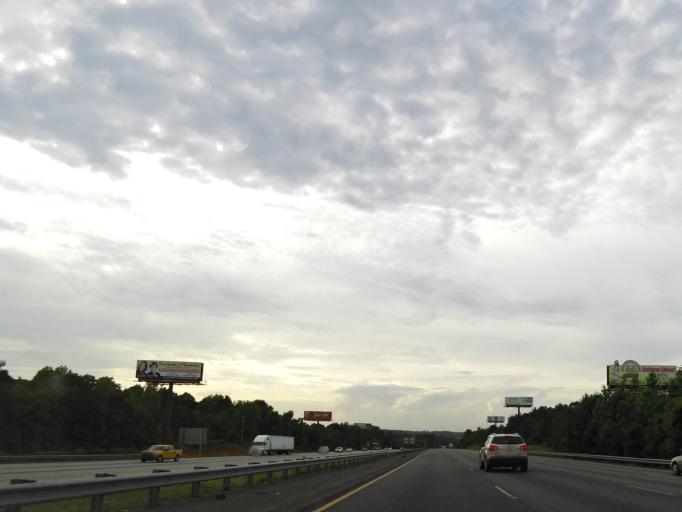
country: US
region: Georgia
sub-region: Monroe County
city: Forsyth
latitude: 32.9670
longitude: -83.8214
